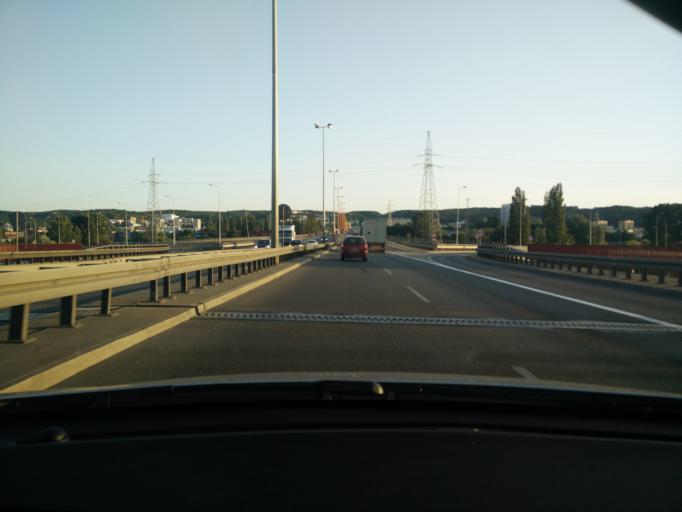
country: PL
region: Pomeranian Voivodeship
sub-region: Gdynia
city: Pogorze
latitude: 54.5432
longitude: 18.4989
